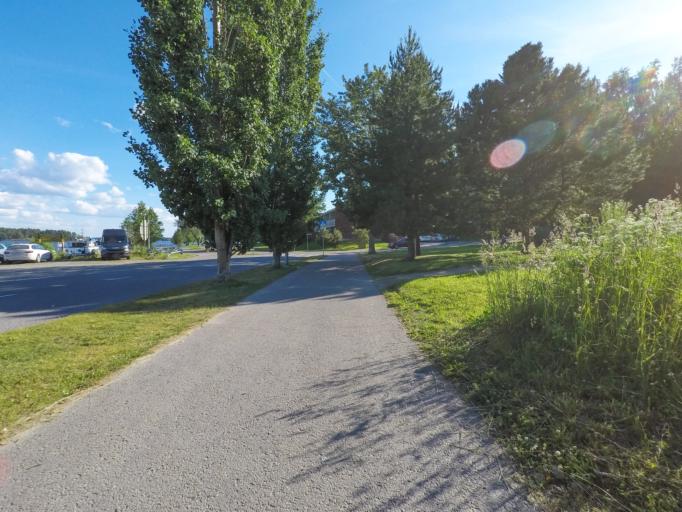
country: FI
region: Southern Savonia
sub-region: Savonlinna
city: Savonlinna
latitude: 61.8660
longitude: 28.8671
